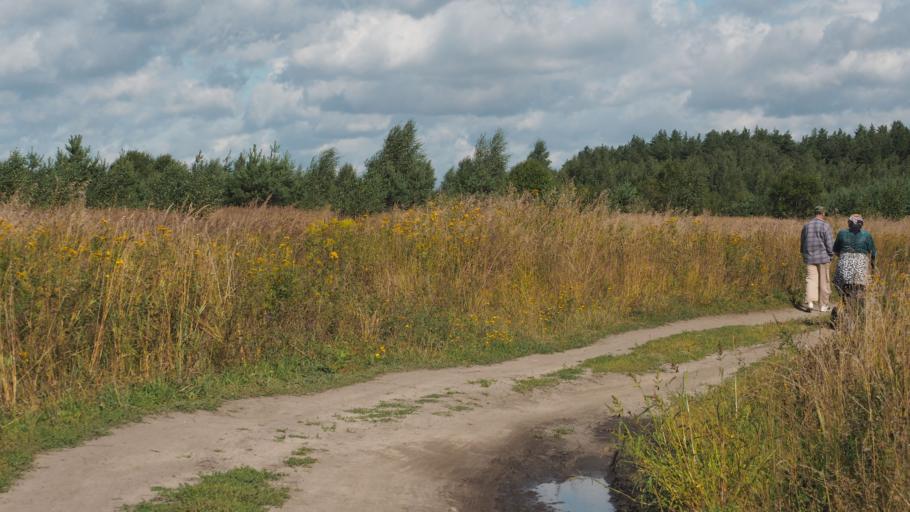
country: RU
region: Moskovskaya
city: Ramenskoye
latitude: 55.5908
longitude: 38.2896
